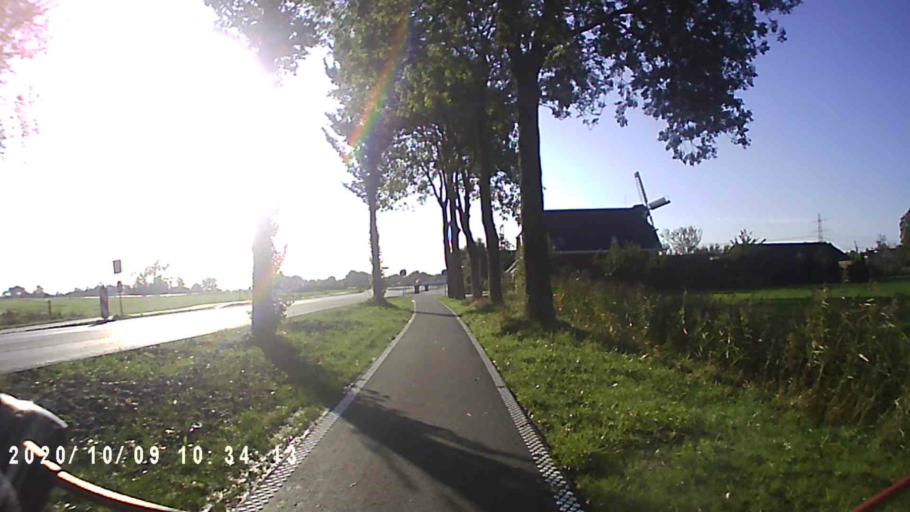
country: NL
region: Groningen
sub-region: Gemeente Winsum
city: Winsum
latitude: 53.3022
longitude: 6.5323
